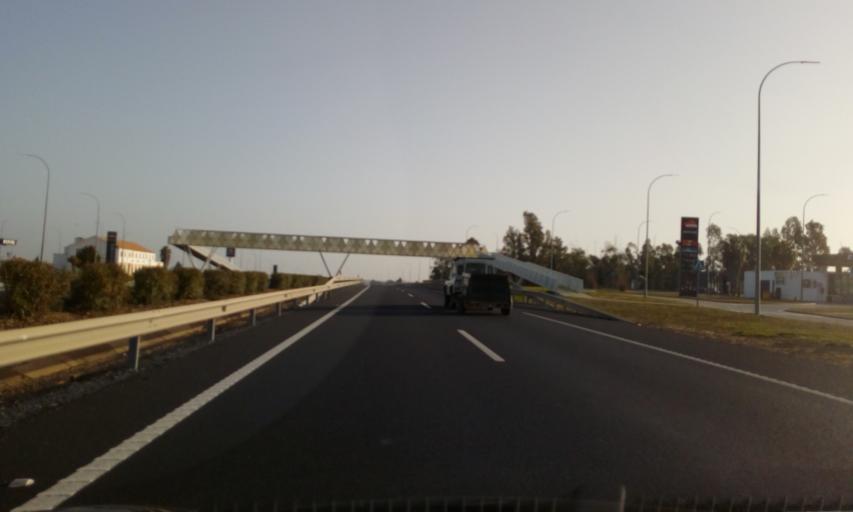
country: ES
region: Andalusia
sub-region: Provincia de Huelva
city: Chucena
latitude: 37.3472
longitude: -6.4245
